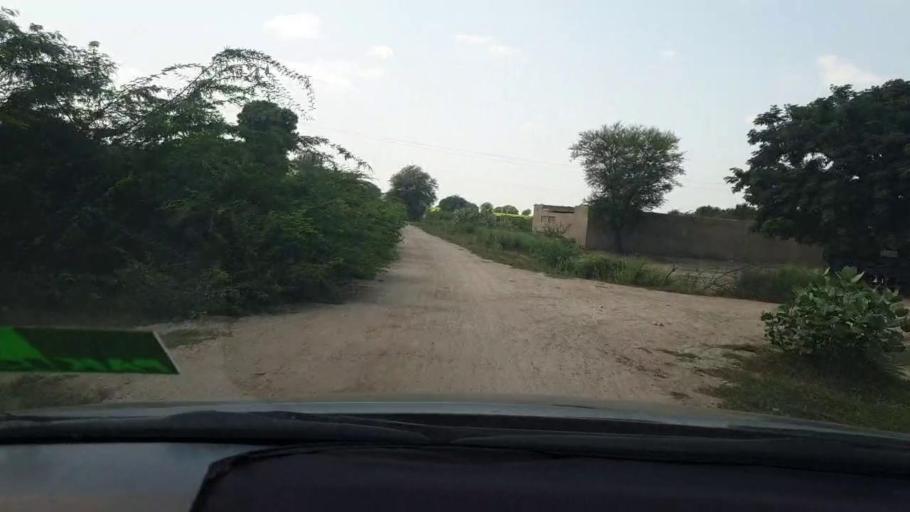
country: PK
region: Sindh
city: Naukot
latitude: 24.9076
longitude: 69.2629
